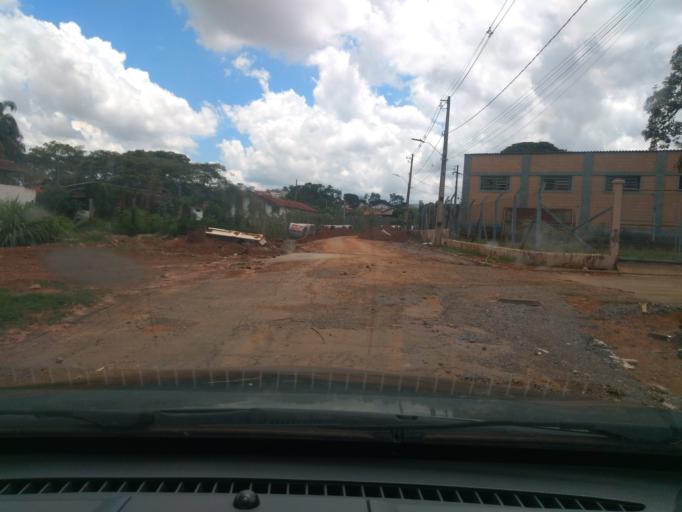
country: BR
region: Minas Gerais
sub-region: Tres Coracoes
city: Tres Coracoes
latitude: -21.6702
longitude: -45.2704
